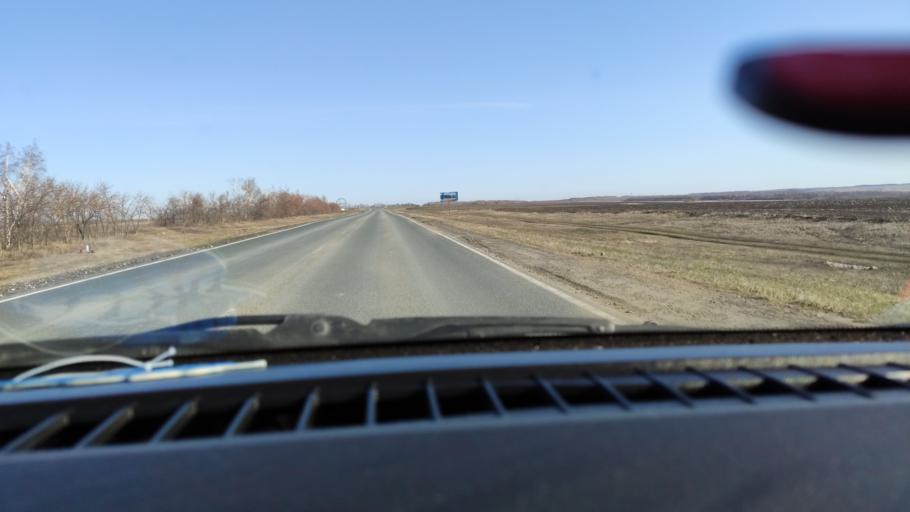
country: RU
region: Saratov
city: Dukhovnitskoye
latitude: 52.7989
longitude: 48.2305
